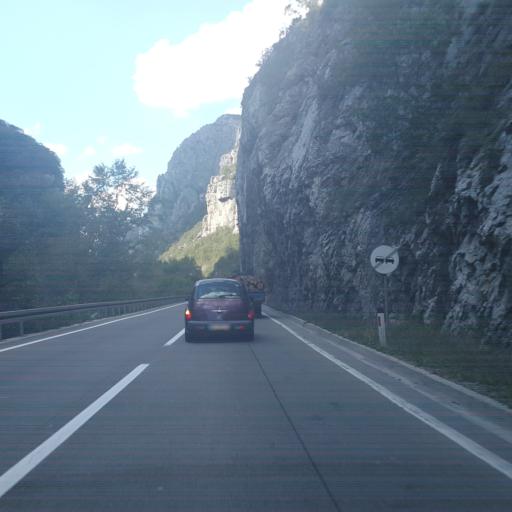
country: RS
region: Central Serbia
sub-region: Nisavski Okrug
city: Svrljig
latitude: 43.3306
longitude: 22.1556
